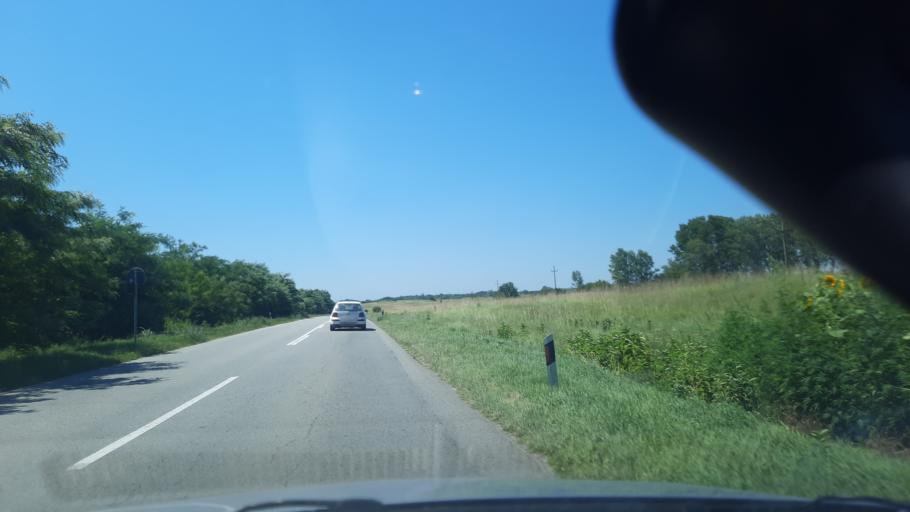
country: RS
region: Central Serbia
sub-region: Branicevski Okrug
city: Pozarevac
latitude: 44.8012
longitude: 21.1861
